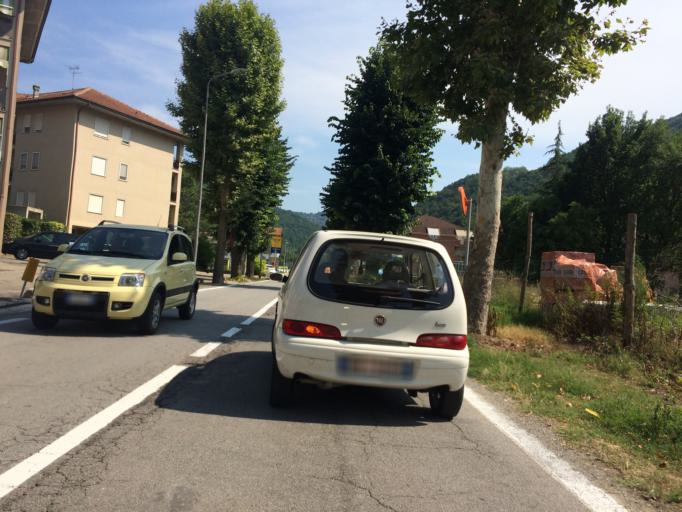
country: IT
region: Piedmont
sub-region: Provincia di Cuneo
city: Cortemilia
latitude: 44.5740
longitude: 8.1999
